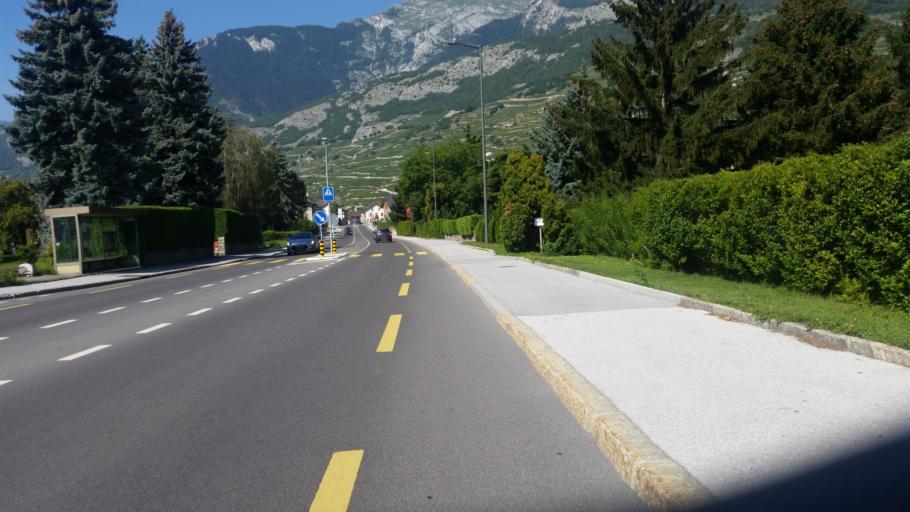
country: CH
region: Valais
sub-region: Conthey District
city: Vetroz
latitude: 46.2259
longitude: 7.2895
